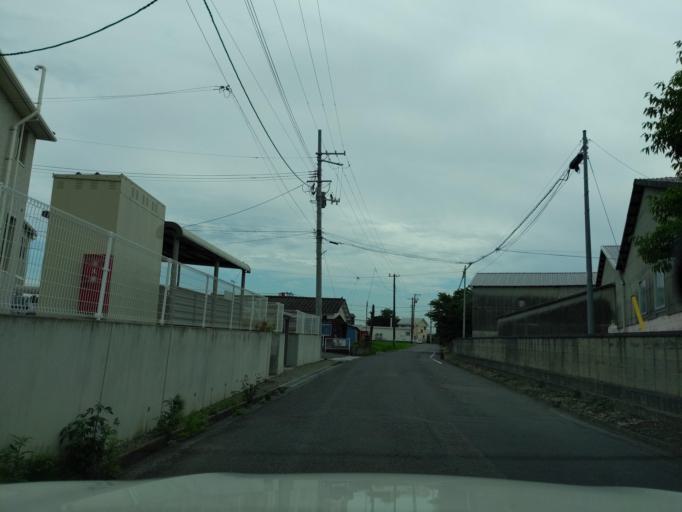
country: JP
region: Fukushima
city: Koriyama
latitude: 37.4195
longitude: 140.4027
